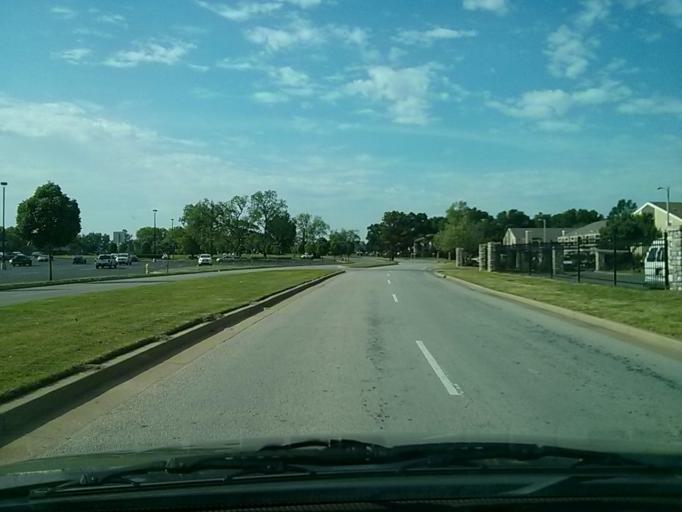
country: US
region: Oklahoma
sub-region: Tulsa County
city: Jenks
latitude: 36.0603
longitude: -95.9635
